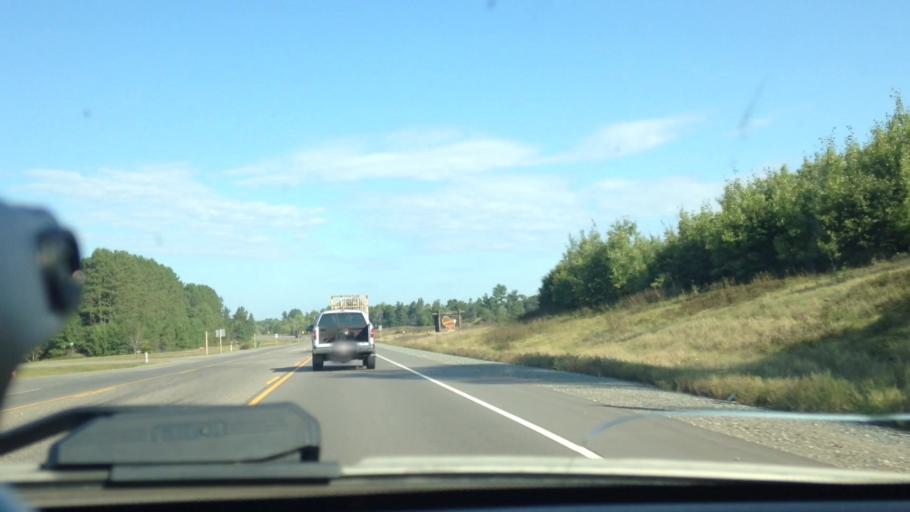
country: US
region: Michigan
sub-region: Dickinson County
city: Iron Mountain
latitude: 45.8704
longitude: -88.0829
